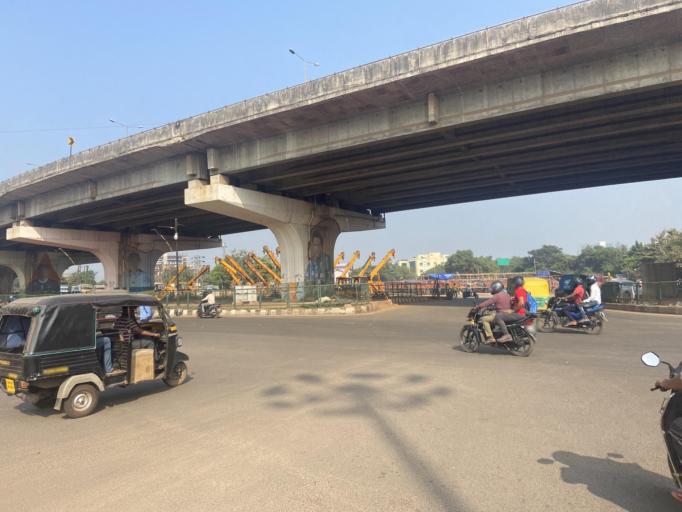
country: IN
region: Odisha
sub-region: Khordha
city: Bhubaneshwar
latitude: 20.2950
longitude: 85.8574
